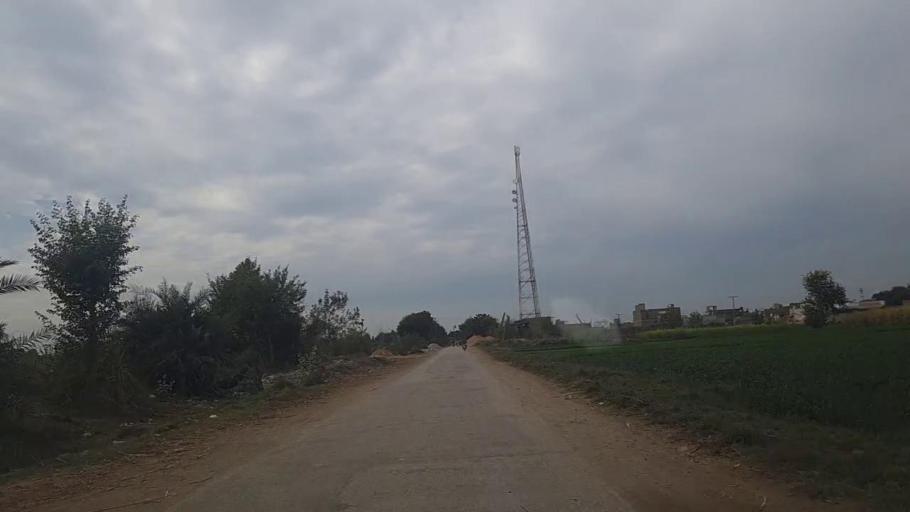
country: PK
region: Sindh
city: Khadro
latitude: 26.1288
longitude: 68.8048
